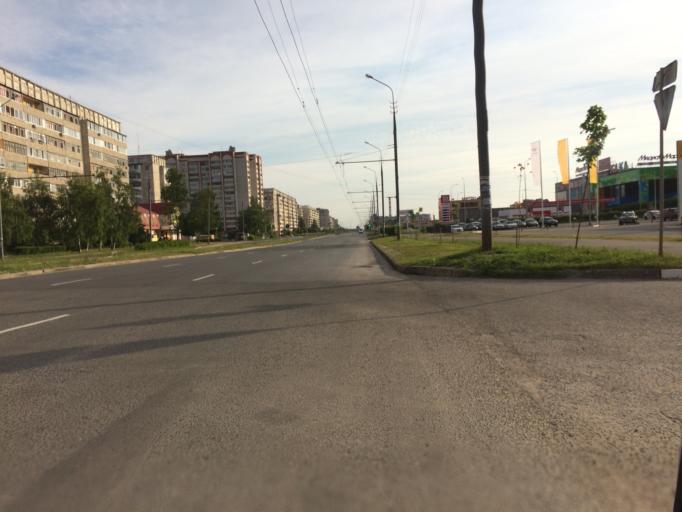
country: RU
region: Mariy-El
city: Yoshkar-Ola
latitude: 56.6264
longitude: 47.9261
